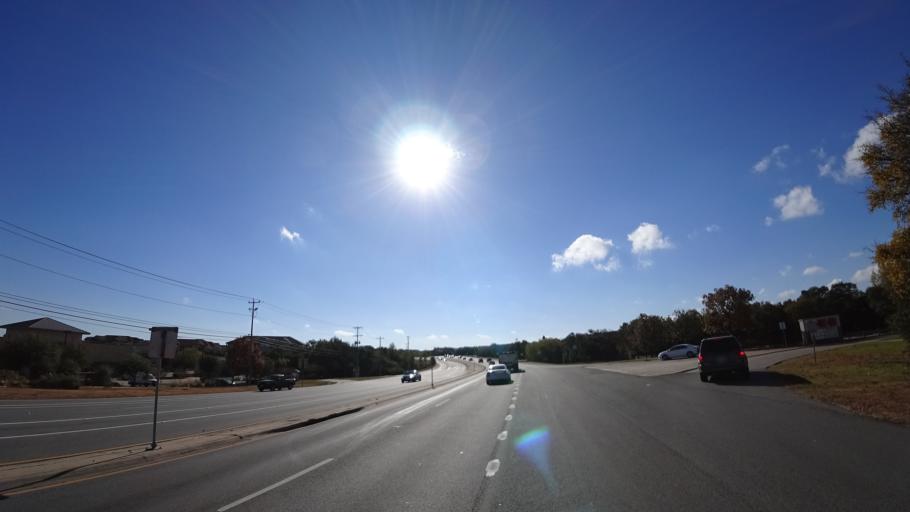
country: US
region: Texas
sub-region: Williamson County
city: Brushy Creek
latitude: 30.5338
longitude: -97.7824
